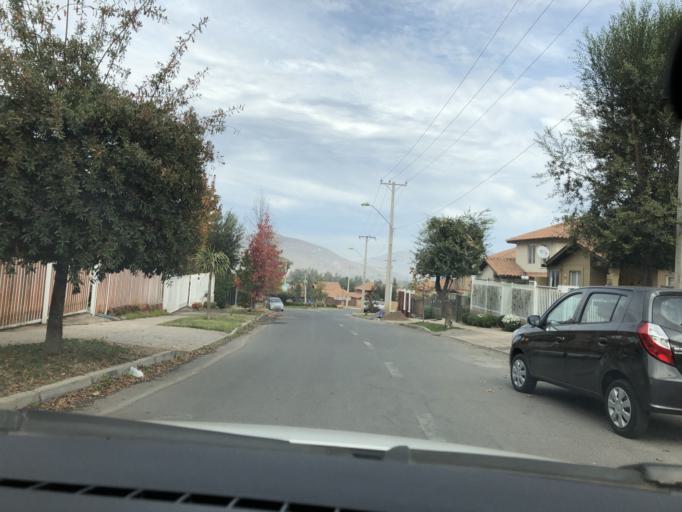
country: CL
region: Santiago Metropolitan
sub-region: Provincia de Cordillera
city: Puente Alto
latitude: -33.5825
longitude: -70.5136
